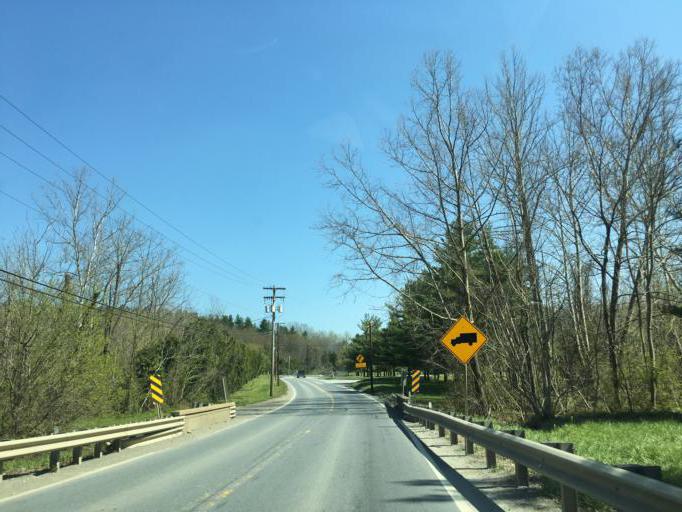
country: US
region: Maryland
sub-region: Frederick County
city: Woodsboro
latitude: 39.5273
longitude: -77.3002
